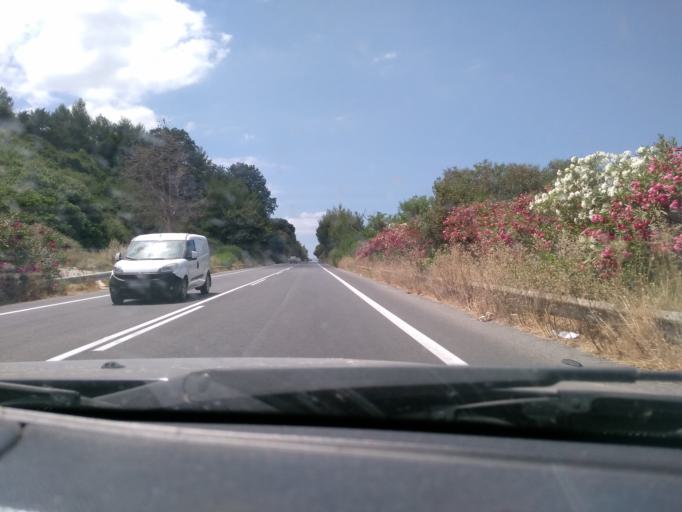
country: GR
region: Crete
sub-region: Nomos Chanias
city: Georgioupolis
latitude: 35.3619
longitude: 24.2462
